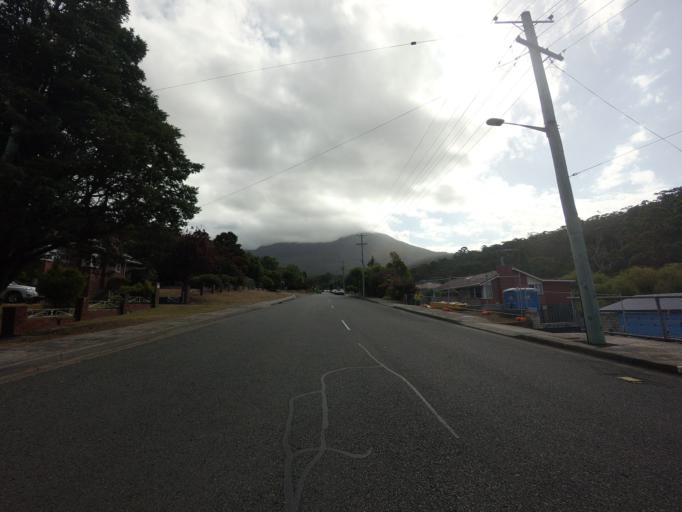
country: AU
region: Tasmania
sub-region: Hobart
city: Dynnyrne
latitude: -42.8980
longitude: 147.2899
